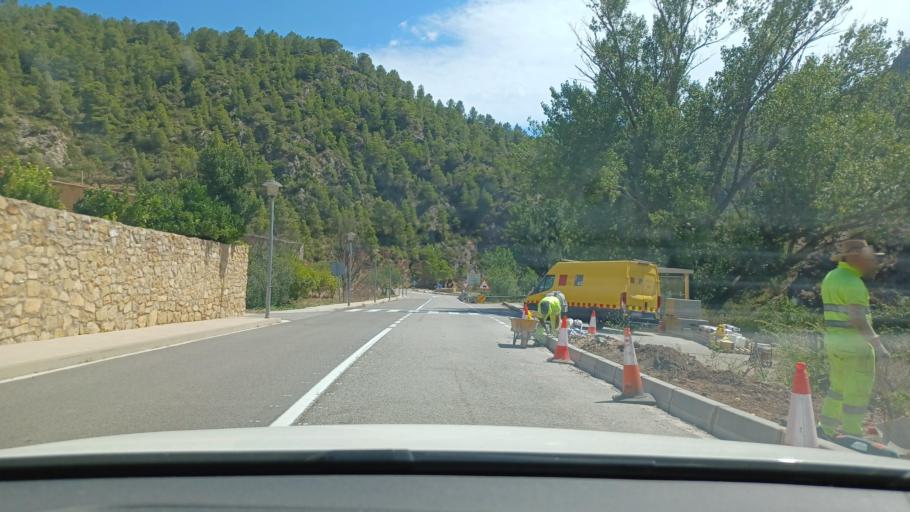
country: ES
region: Catalonia
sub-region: Provincia de Tarragona
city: Bot
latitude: 40.9820
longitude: 0.4062
